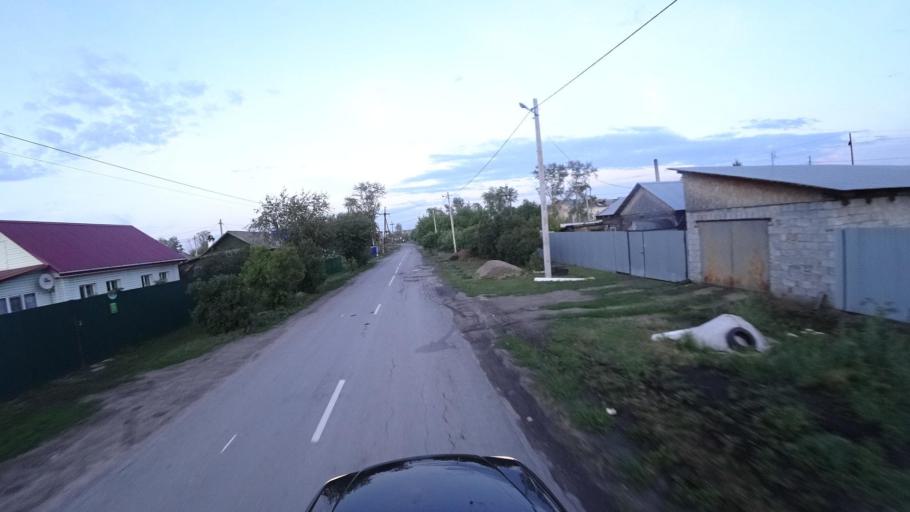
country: RU
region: Sverdlovsk
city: Kamyshlov
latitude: 56.8497
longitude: 62.7319
